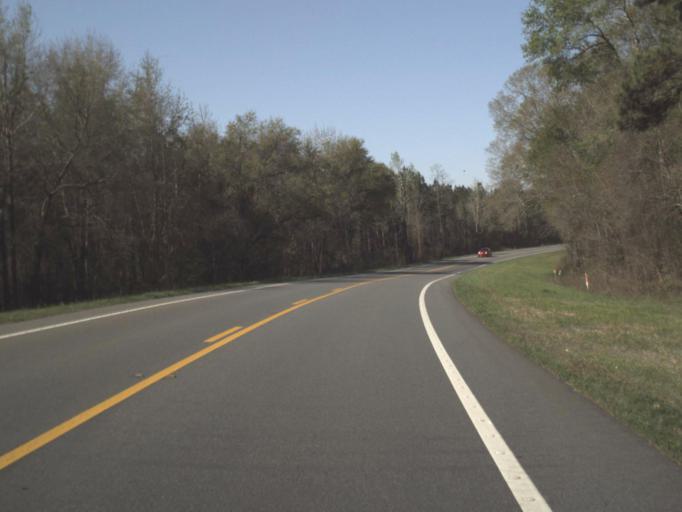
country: US
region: Alabama
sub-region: Houston County
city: Cottonwood
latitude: 30.9352
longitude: -85.2982
